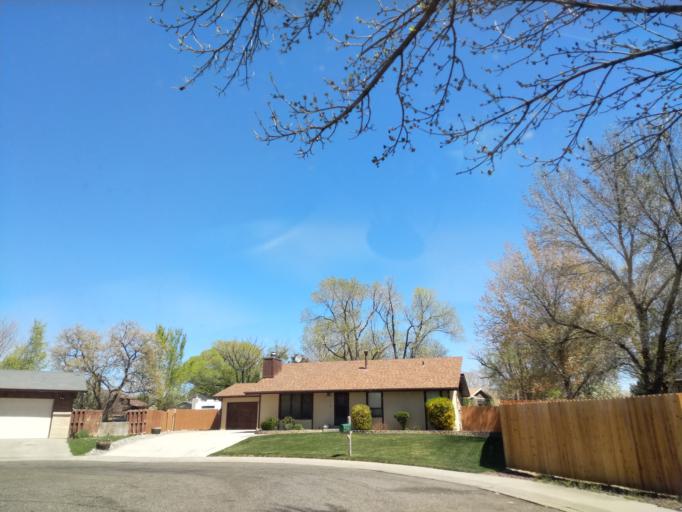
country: US
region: Colorado
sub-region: Mesa County
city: Grand Junction
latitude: 39.0949
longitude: -108.5402
